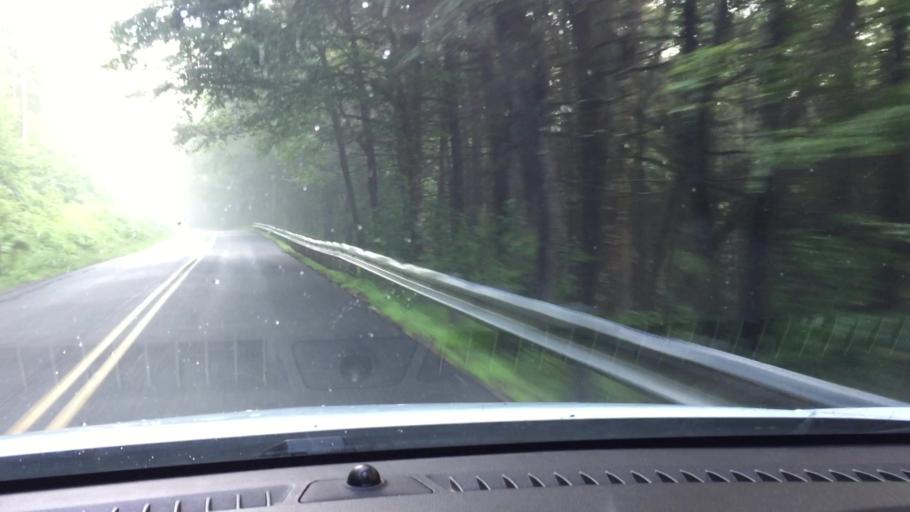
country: US
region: Massachusetts
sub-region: Berkshire County
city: Becket
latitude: 42.4093
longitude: -72.9798
